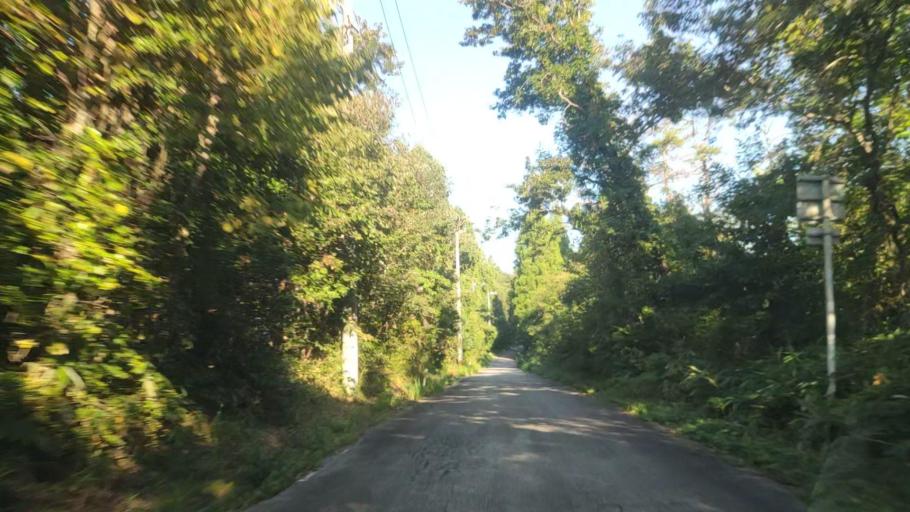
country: JP
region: Ishikawa
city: Nanao
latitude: 37.1342
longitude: 136.9162
